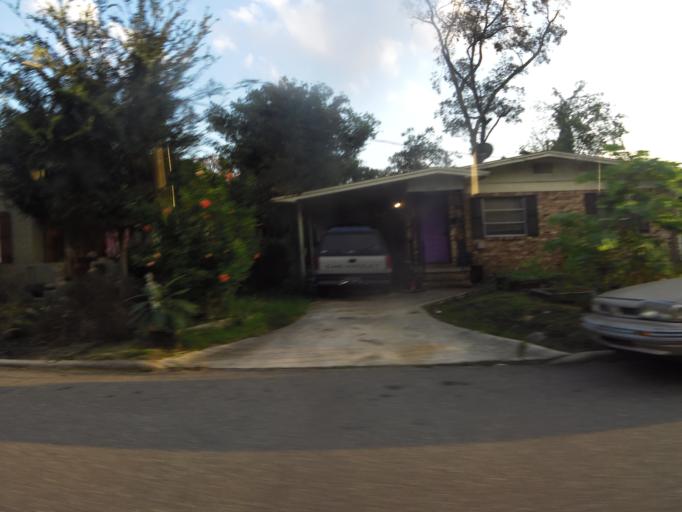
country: US
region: Florida
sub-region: Duval County
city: Jacksonville
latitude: 30.2847
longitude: -81.7149
